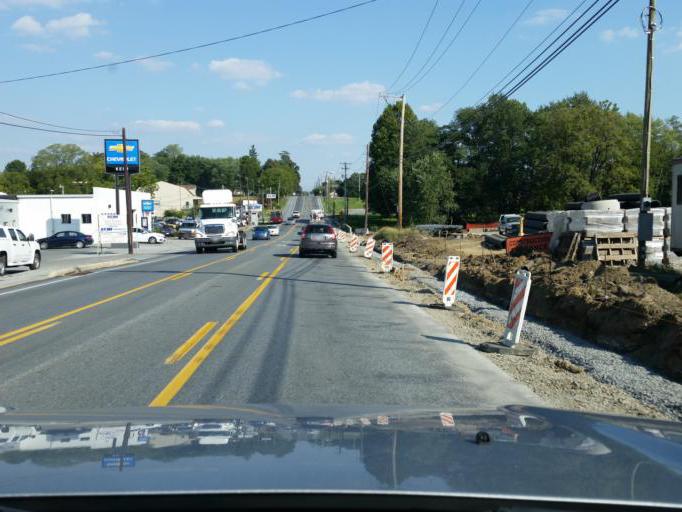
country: US
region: Pennsylvania
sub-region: Lancaster County
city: Paradise
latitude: 40.0063
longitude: -76.1120
